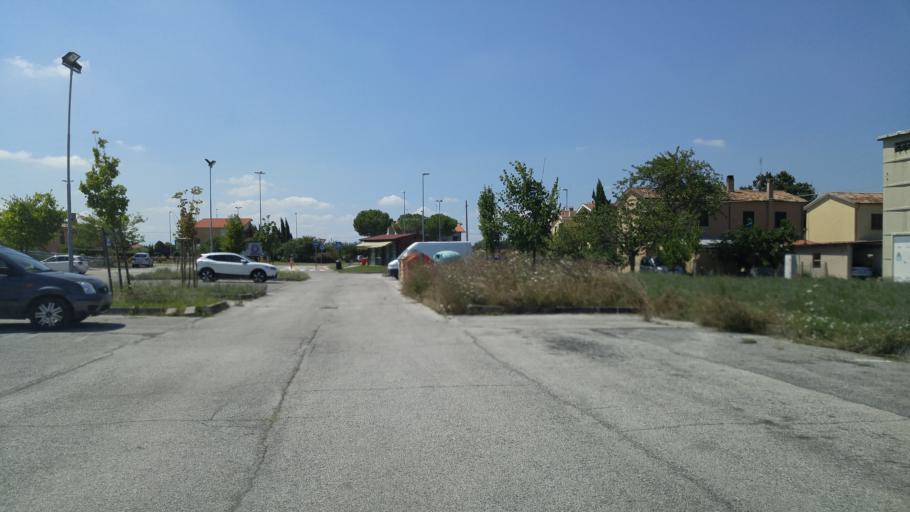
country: IT
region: The Marches
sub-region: Provincia di Pesaro e Urbino
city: Rosciano
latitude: 43.8031
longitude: 12.9921
